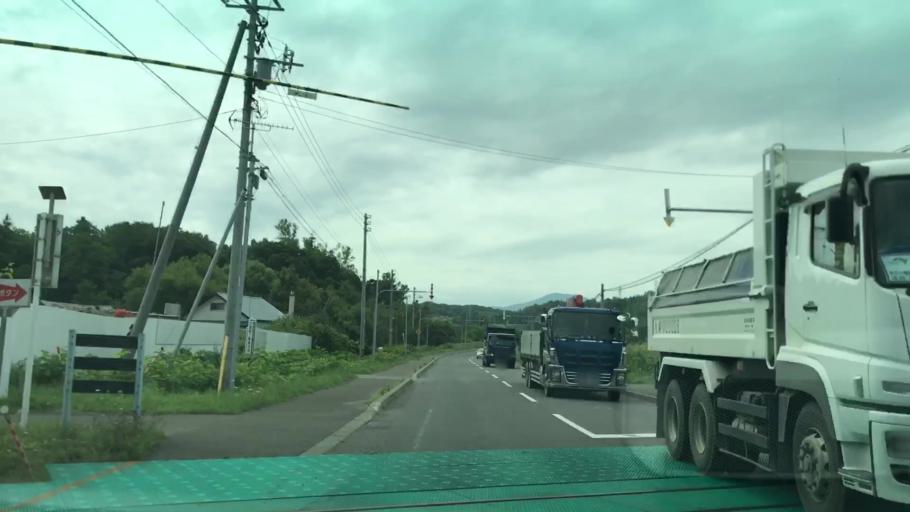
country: JP
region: Hokkaido
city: Yoichi
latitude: 43.1952
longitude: 140.8440
